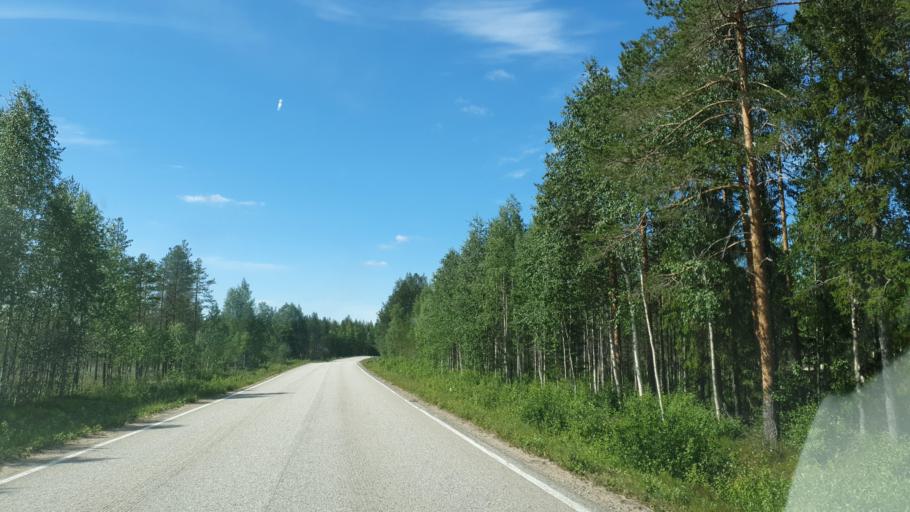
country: FI
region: Kainuu
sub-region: Kehys-Kainuu
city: Suomussalmi
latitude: 64.5670
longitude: 28.9806
